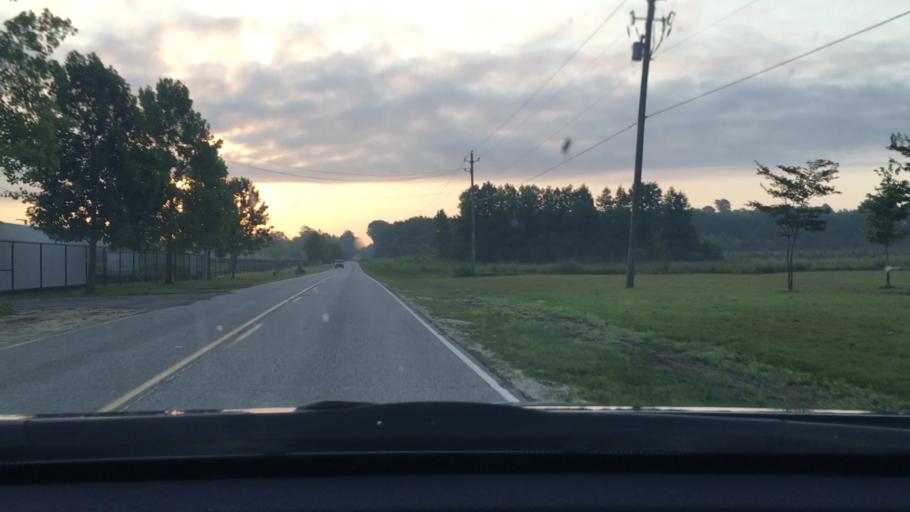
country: US
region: South Carolina
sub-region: Darlington County
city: Hartsville
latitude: 34.3501
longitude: -80.0919
